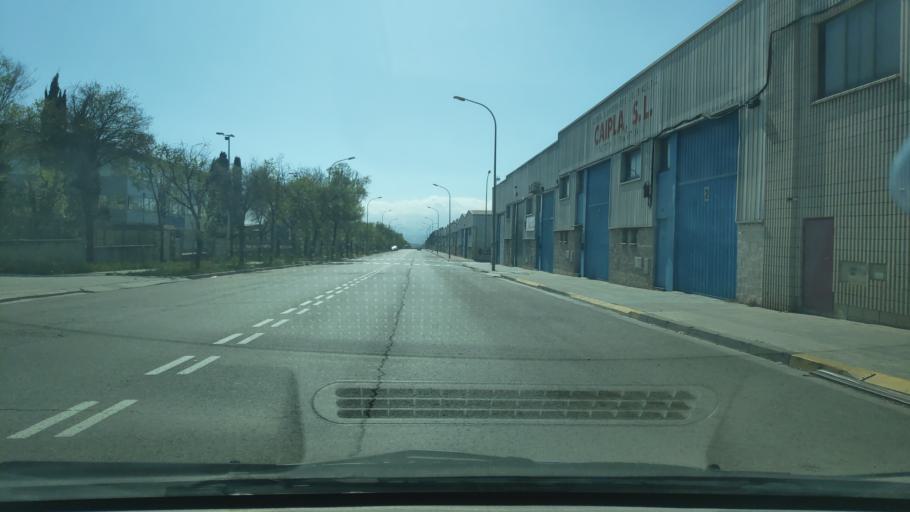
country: ES
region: Catalonia
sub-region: Provincia de Barcelona
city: Polinya
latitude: 41.5413
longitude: 2.1325
